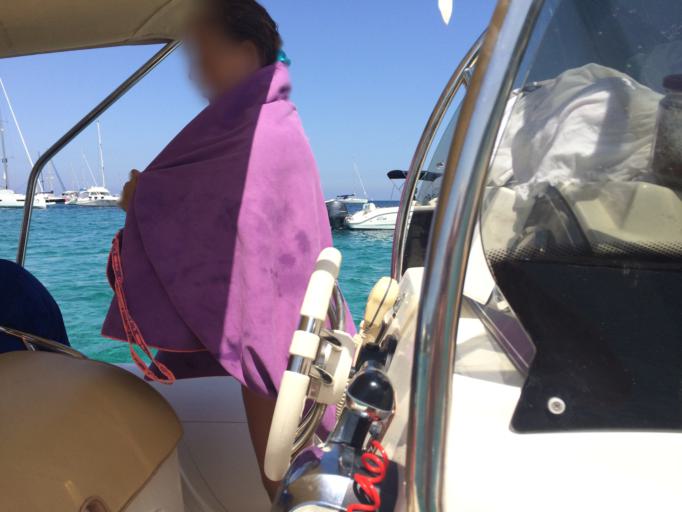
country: FR
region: Corsica
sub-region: Departement de la Haute-Corse
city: Brando
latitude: 43.0071
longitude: 9.4128
